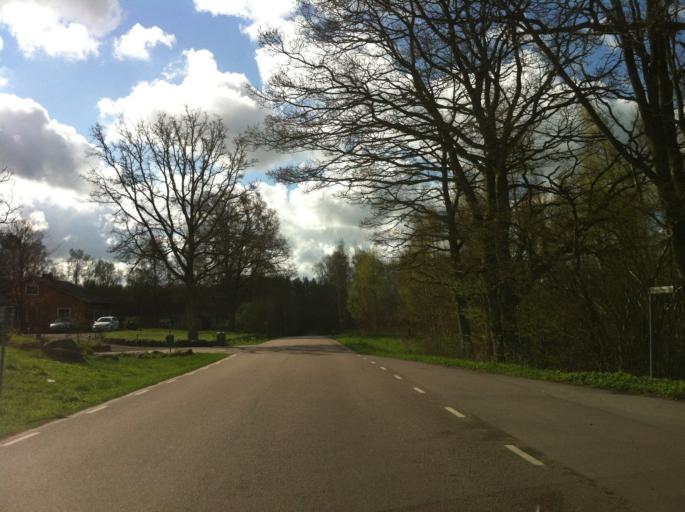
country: SE
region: Skane
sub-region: Horby Kommun
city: Hoerby
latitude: 55.8960
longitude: 13.6122
